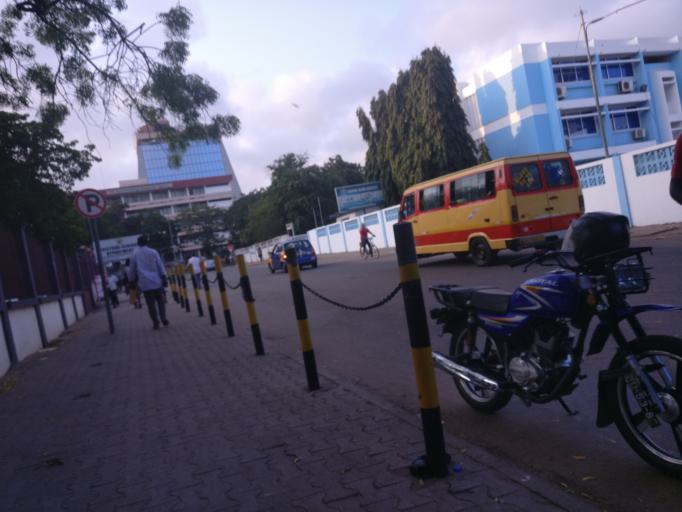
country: GH
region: Greater Accra
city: Accra
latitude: 5.5502
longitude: -0.1997
